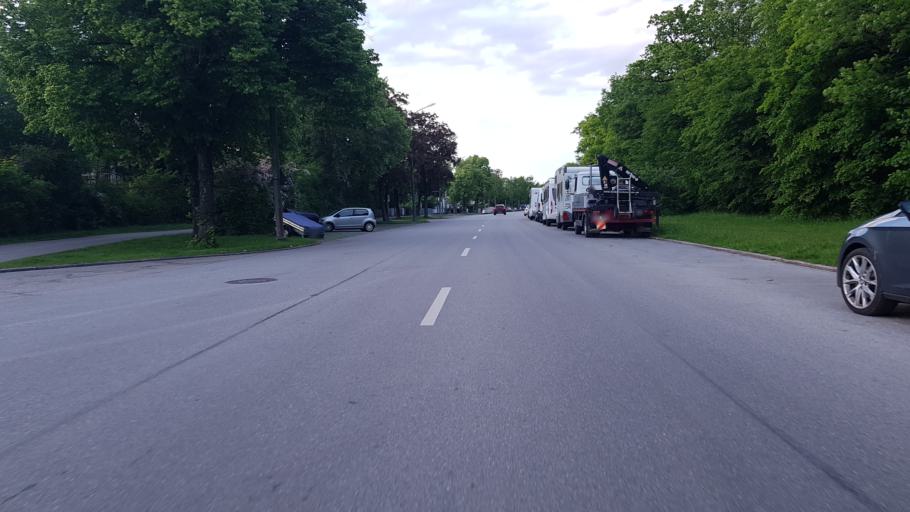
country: DE
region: Bavaria
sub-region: Upper Bavaria
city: Neuried
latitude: 48.1041
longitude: 11.4886
